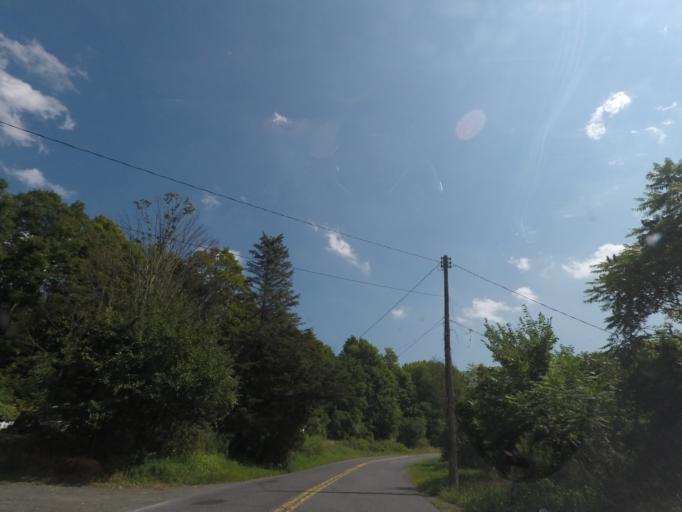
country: US
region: New York
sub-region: Saratoga County
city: Waterford
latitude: 42.8091
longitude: -73.5920
